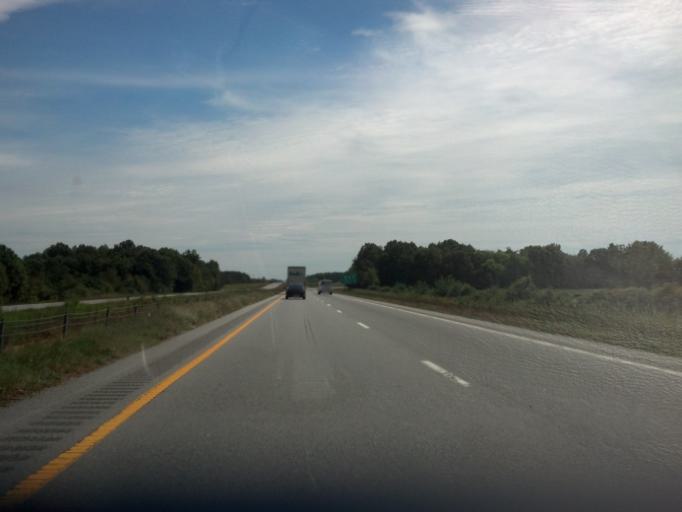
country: US
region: North Carolina
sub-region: Pitt County
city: Greenville
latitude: 35.6614
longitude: -77.3754
